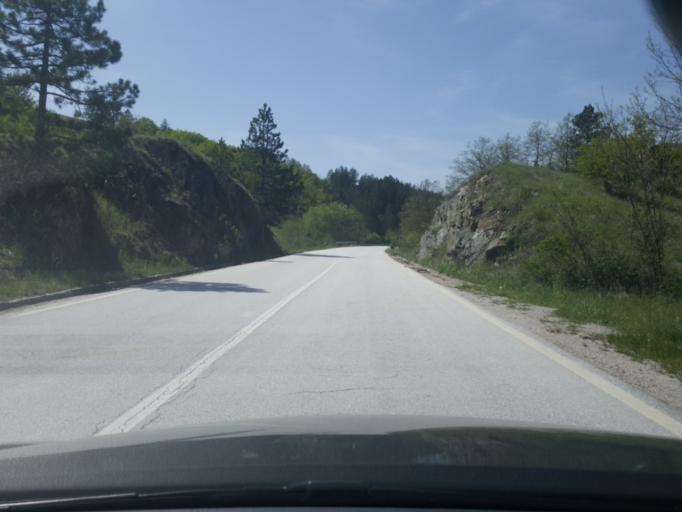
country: RS
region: Central Serbia
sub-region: Zlatiborski Okrug
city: Cajetina
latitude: 43.7908
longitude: 19.6598
